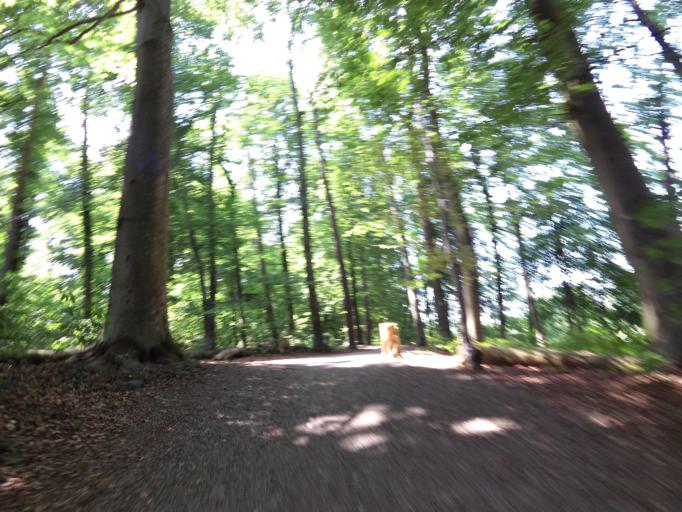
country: CH
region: Aargau
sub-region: Bezirk Baden
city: Spreitenbach
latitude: 47.4285
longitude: 8.3795
